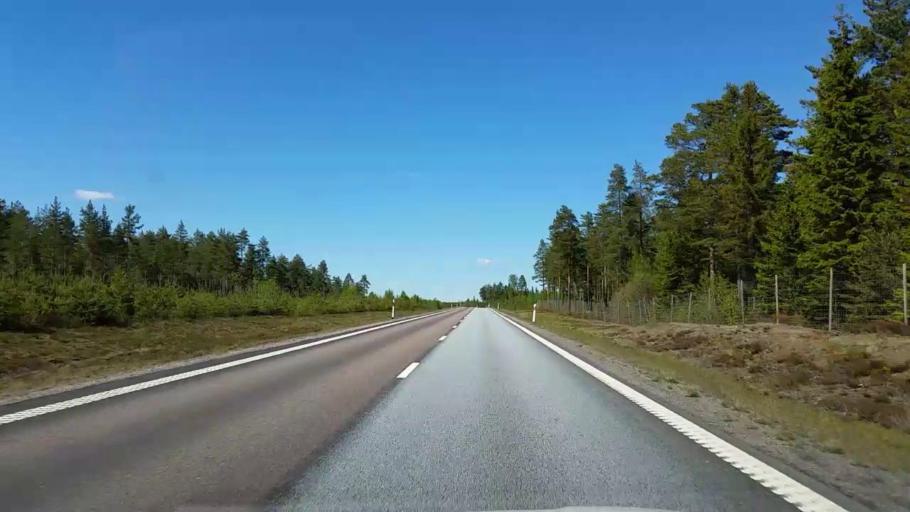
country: SE
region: Gaevleborg
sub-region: Soderhamns Kommun
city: Soderhamn
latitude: 61.3881
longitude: 16.9925
